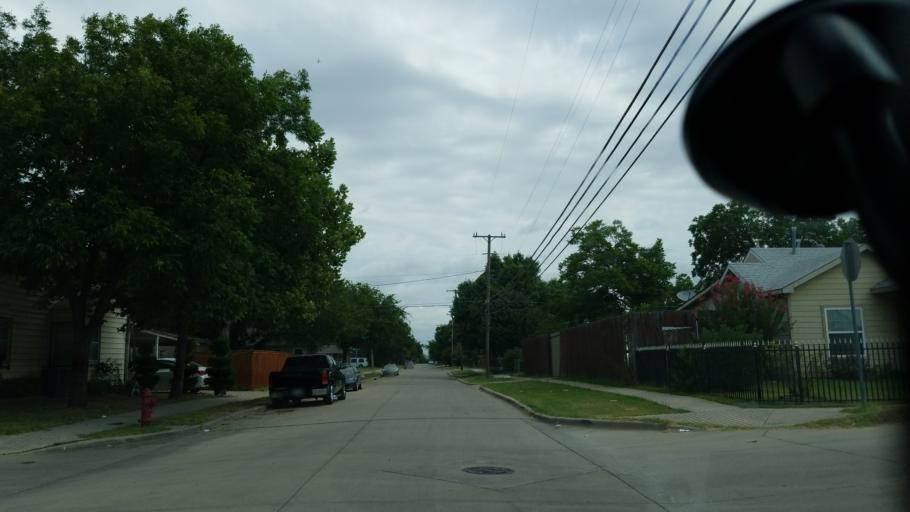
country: US
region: Texas
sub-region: Dallas County
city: Grand Prairie
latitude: 32.7504
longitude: -96.9842
